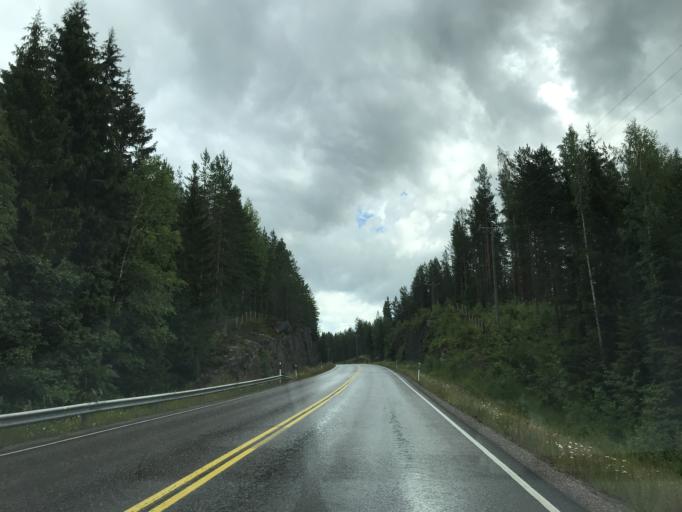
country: FI
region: Uusimaa
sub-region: Porvoo
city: Pukkila
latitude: 60.7689
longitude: 25.5024
